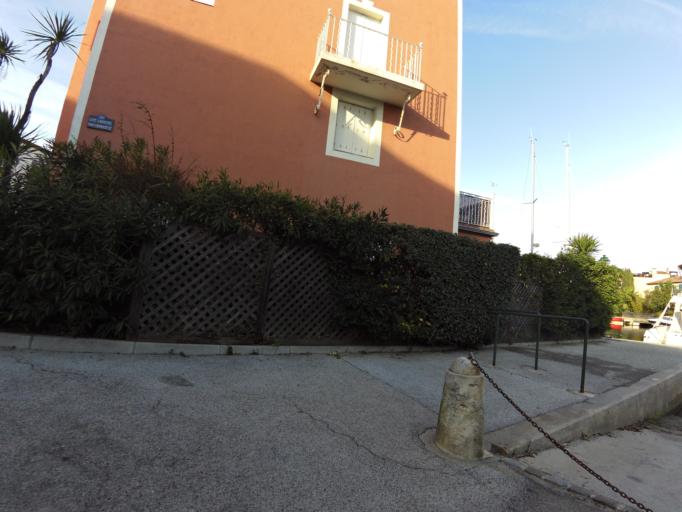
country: FR
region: Provence-Alpes-Cote d'Azur
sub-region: Departement du Var
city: Gassin
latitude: 43.2701
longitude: 6.5741
